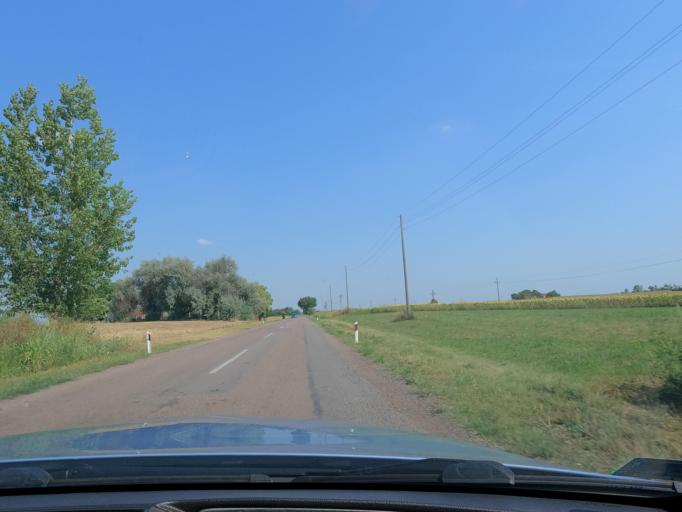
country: RS
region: Autonomna Pokrajina Vojvodina
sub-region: Severnobacki Okrug
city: Mali Igos
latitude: 45.7535
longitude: 19.7824
